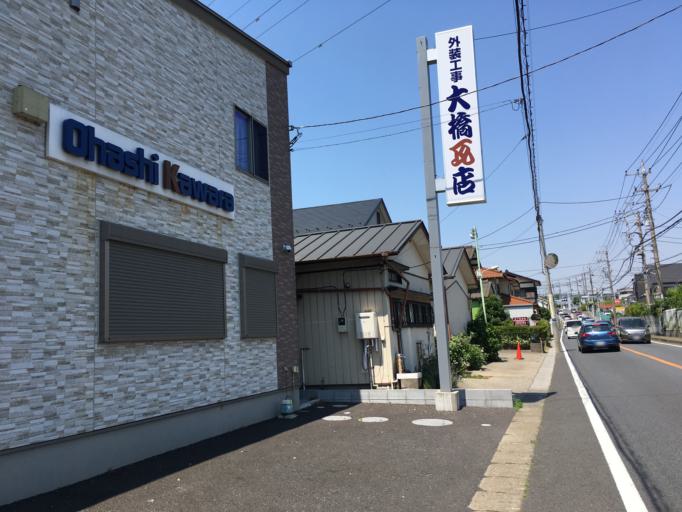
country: JP
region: Chiba
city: Matsudo
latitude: 35.7709
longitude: 139.9193
